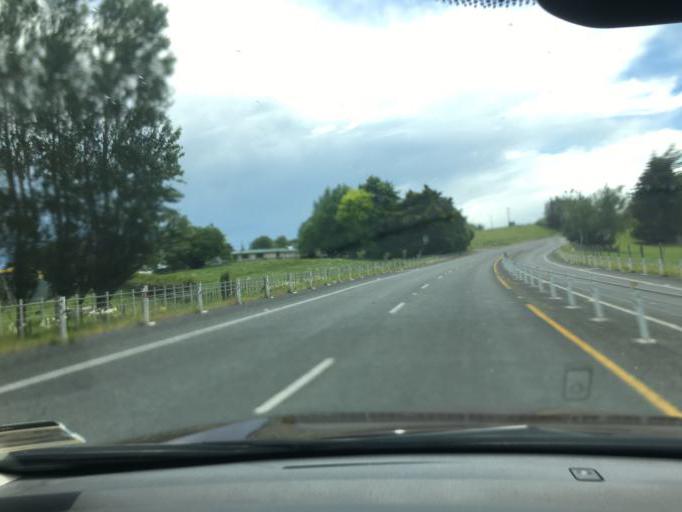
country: NZ
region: Waikato
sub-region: Waipa District
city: Cambridge
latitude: -37.9509
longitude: 175.3143
